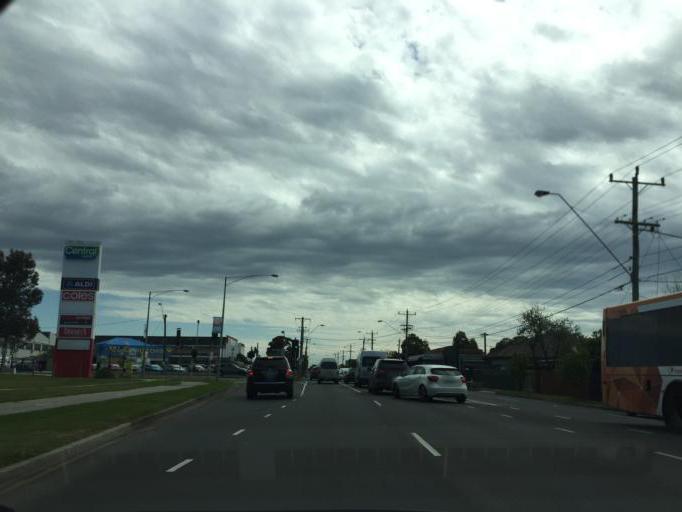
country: AU
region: Victoria
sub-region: Maribyrnong
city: Braybrook
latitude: -37.7935
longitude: 144.8631
